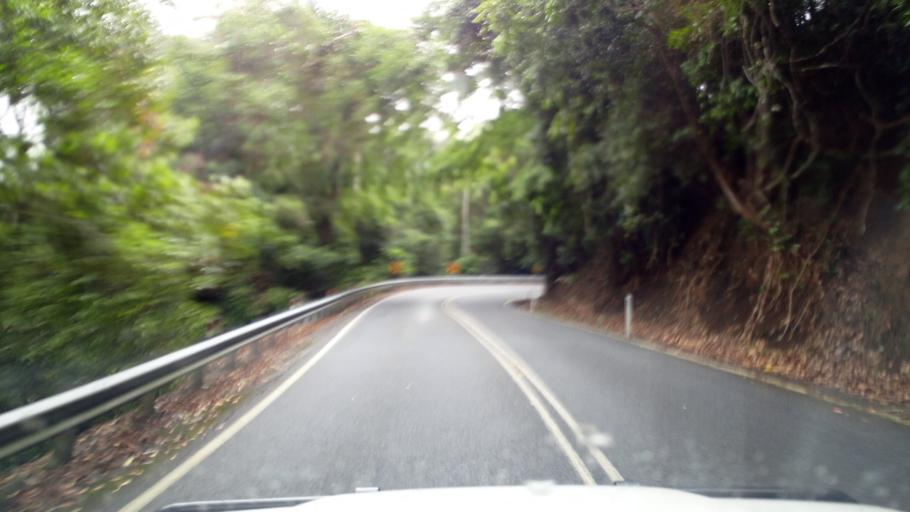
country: AU
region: Queensland
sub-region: Tablelands
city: Tolga
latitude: -17.2188
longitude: 145.6964
